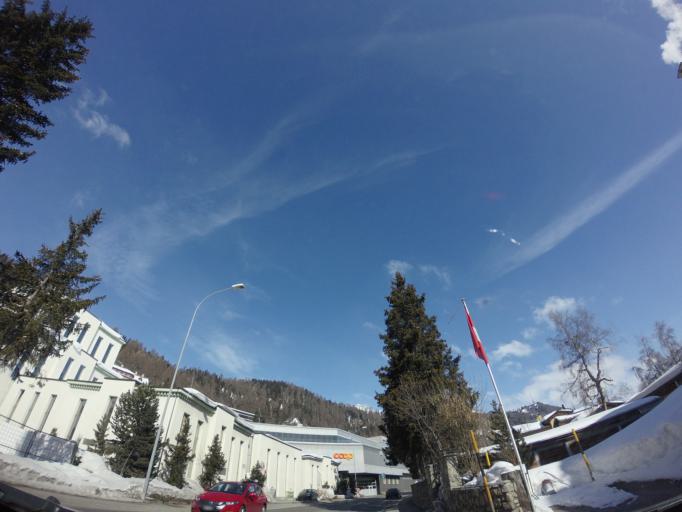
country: CH
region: Grisons
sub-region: Maloja District
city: Saint Moritz
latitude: 46.4896
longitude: 9.8357
